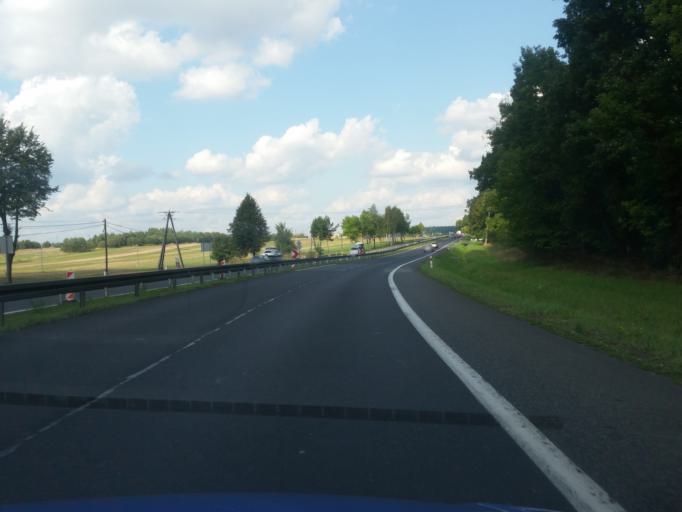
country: PL
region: Silesian Voivodeship
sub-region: Powiat myszkowski
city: Kozieglowy
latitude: 50.5418
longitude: 19.1809
